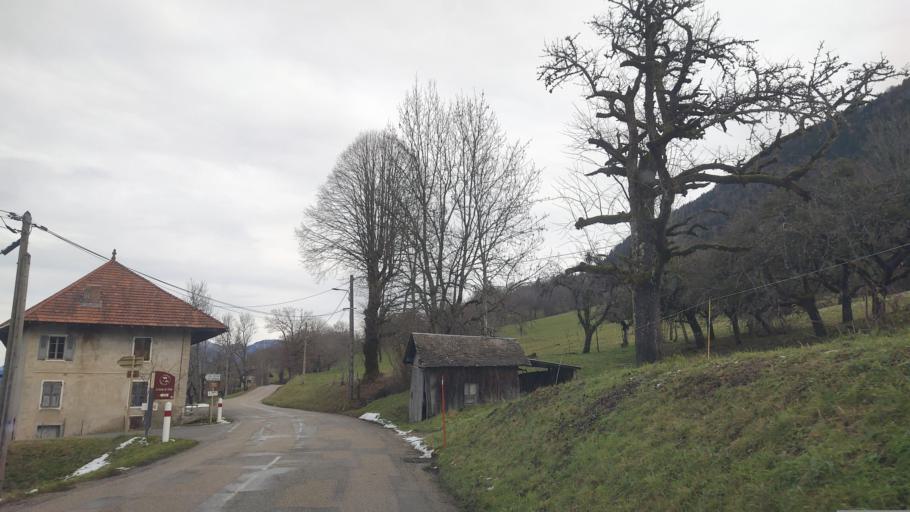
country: FR
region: Rhone-Alpes
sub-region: Departement de la Haute-Savoie
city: Cusy
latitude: 45.6859
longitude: 6.0718
